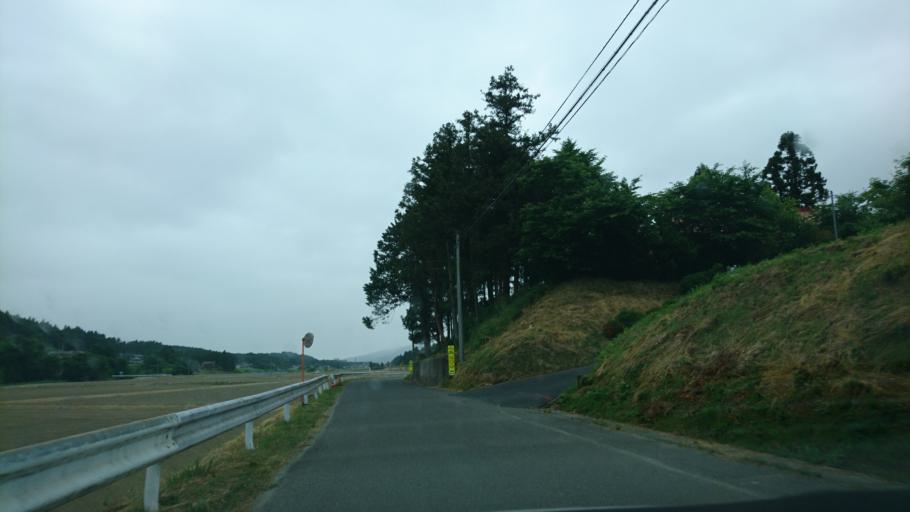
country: JP
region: Iwate
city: Ichinoseki
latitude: 38.9099
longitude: 141.1798
